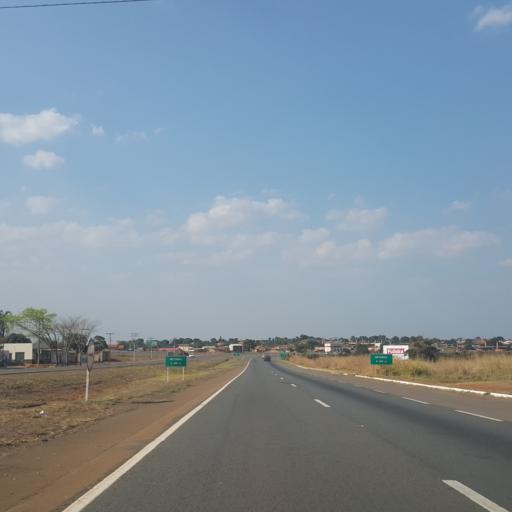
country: BR
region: Goias
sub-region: Abadiania
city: Abadiania
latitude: -16.1909
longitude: -48.7246
